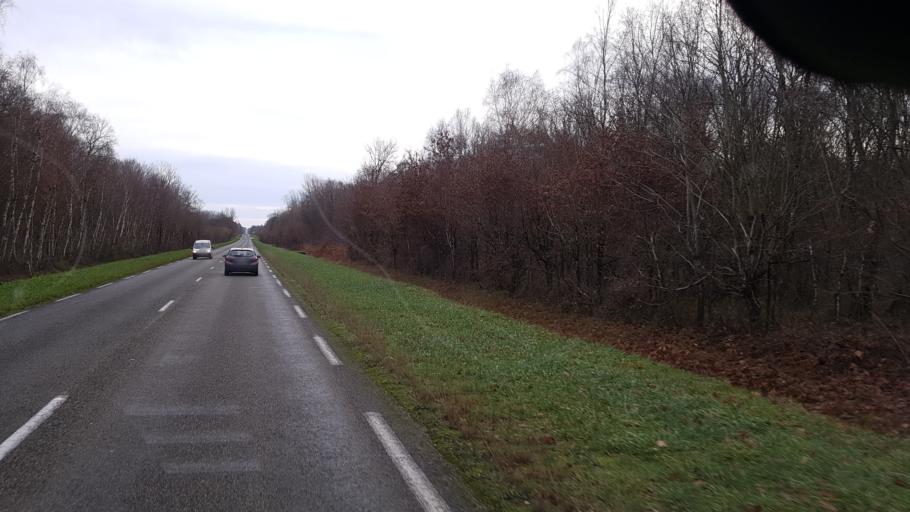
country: FR
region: Centre
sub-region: Departement du Loiret
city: La Ferte-Saint-Aubin
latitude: 47.6978
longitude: 1.9510
